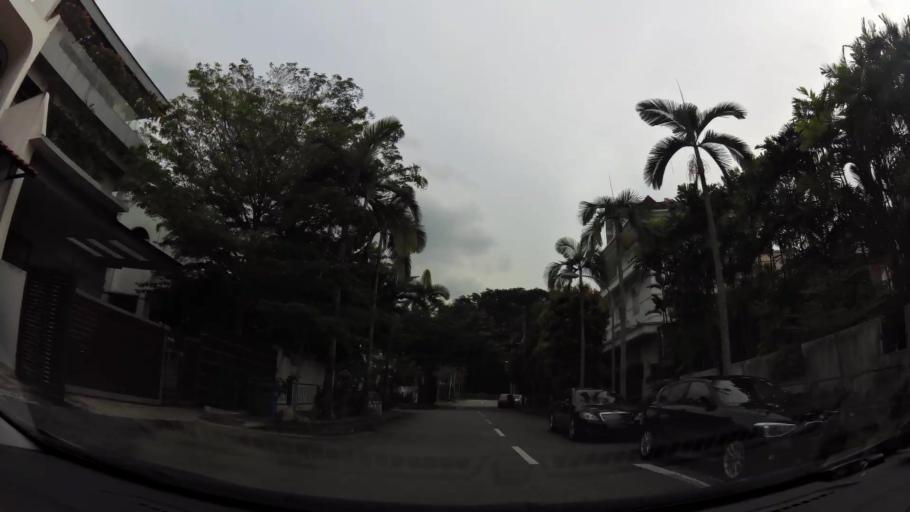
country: MY
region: Johor
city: Kampung Pasir Gudang Baru
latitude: 1.3988
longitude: 103.8256
